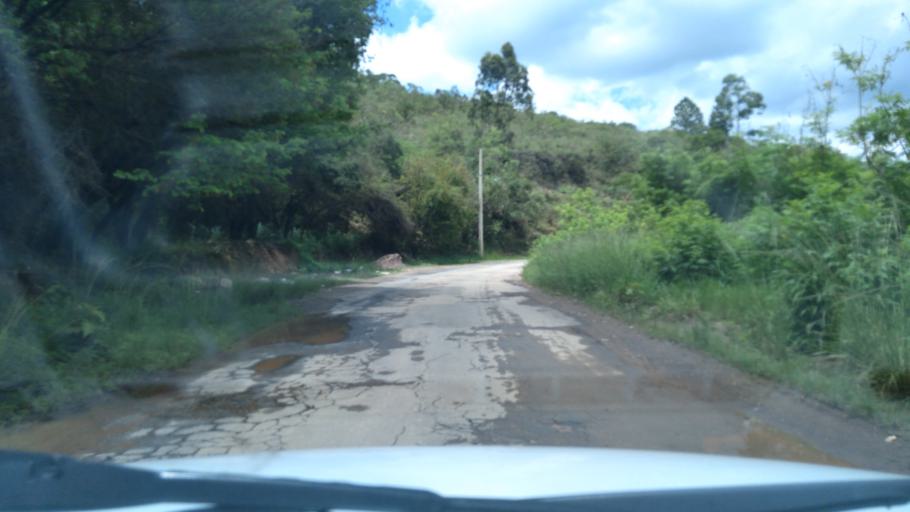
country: BR
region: Minas Gerais
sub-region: Belo Horizonte
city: Belo Horizonte
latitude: -19.9247
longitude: -43.8780
